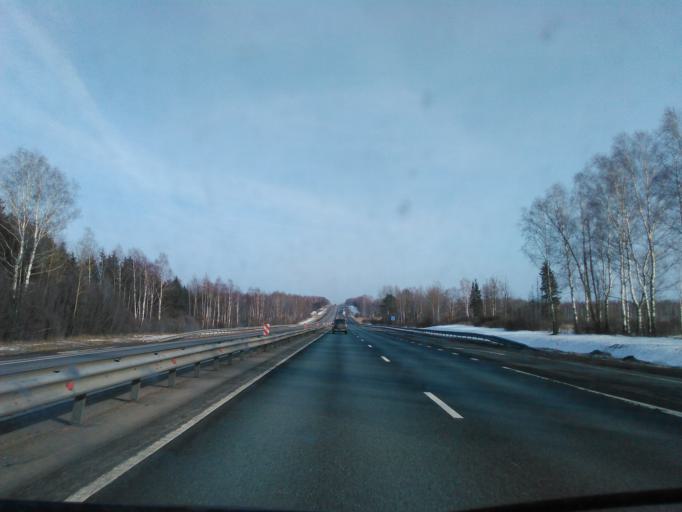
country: RU
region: Smolensk
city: Verkhnedneprovskiy
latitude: 55.1824
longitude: 33.5309
